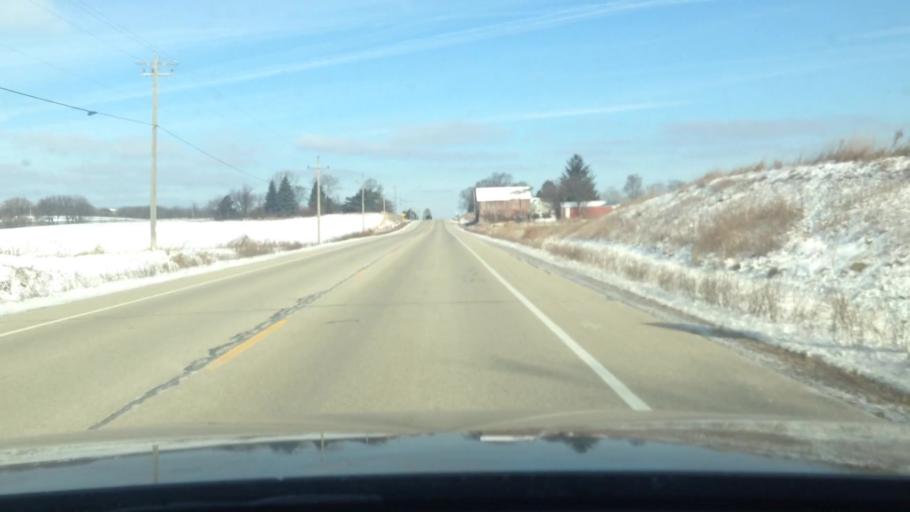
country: US
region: Wisconsin
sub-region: Walworth County
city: East Troy
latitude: 42.7636
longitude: -88.4064
